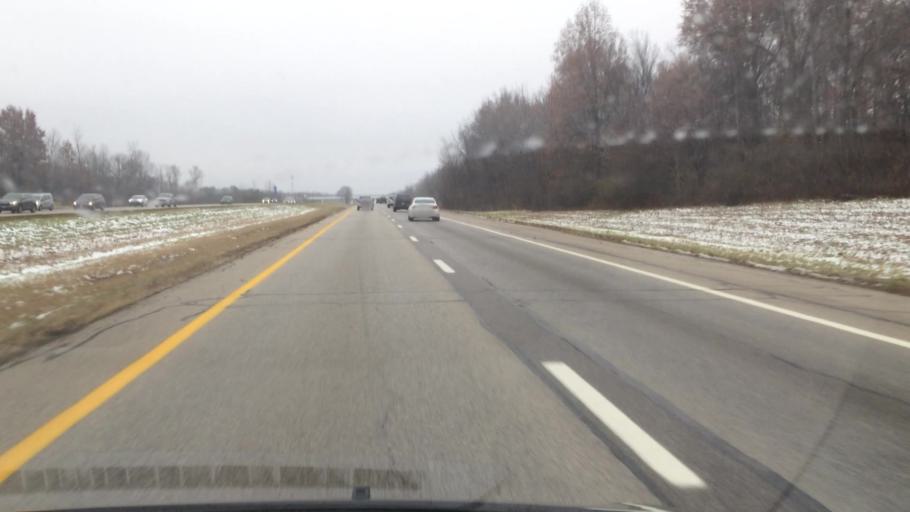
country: US
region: Ohio
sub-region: Summit County
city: Richfield
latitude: 41.2091
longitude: -81.6259
